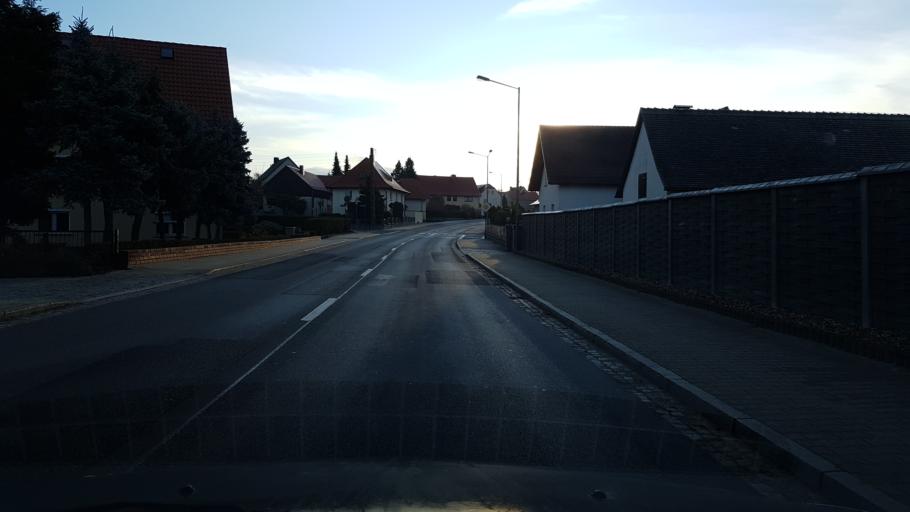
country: DE
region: Saxony
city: Radibor
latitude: 51.2271
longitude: 14.3836
